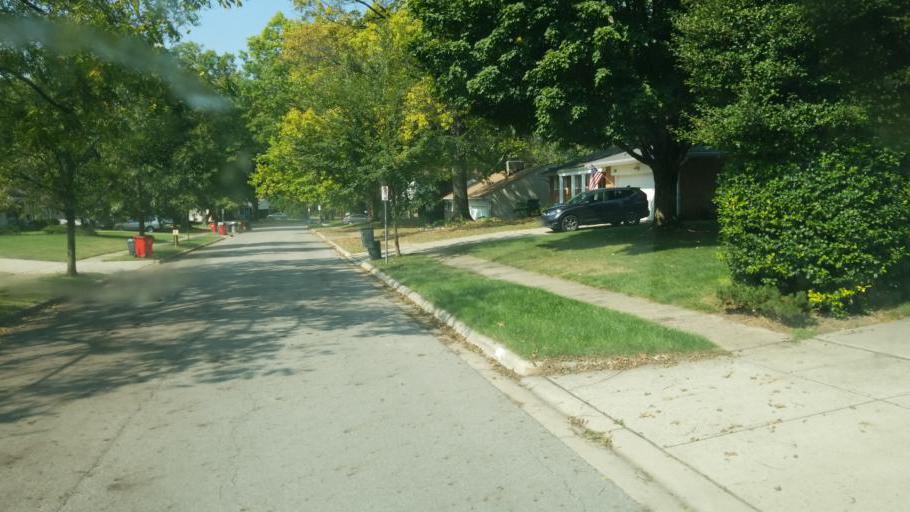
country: US
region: Ohio
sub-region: Franklin County
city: Worthington
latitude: 40.0881
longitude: -83.0251
